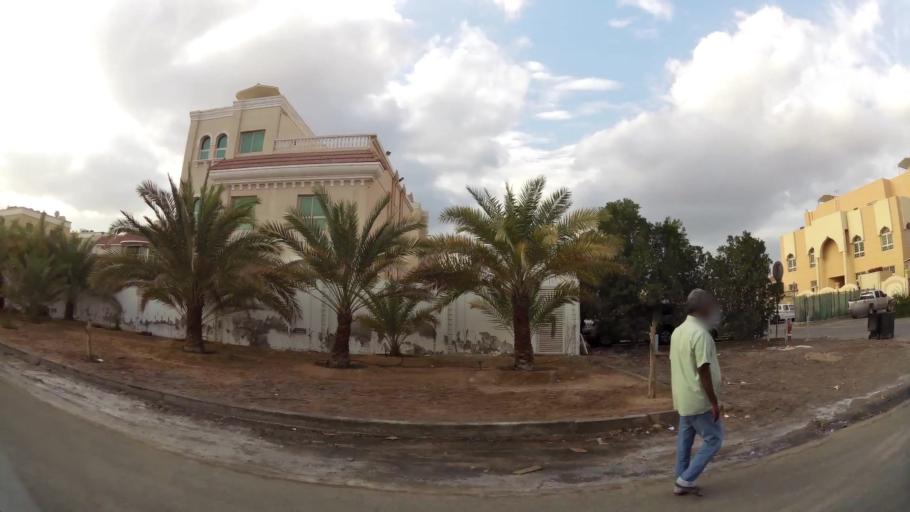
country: AE
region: Abu Dhabi
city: Abu Dhabi
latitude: 24.3651
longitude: 54.5543
